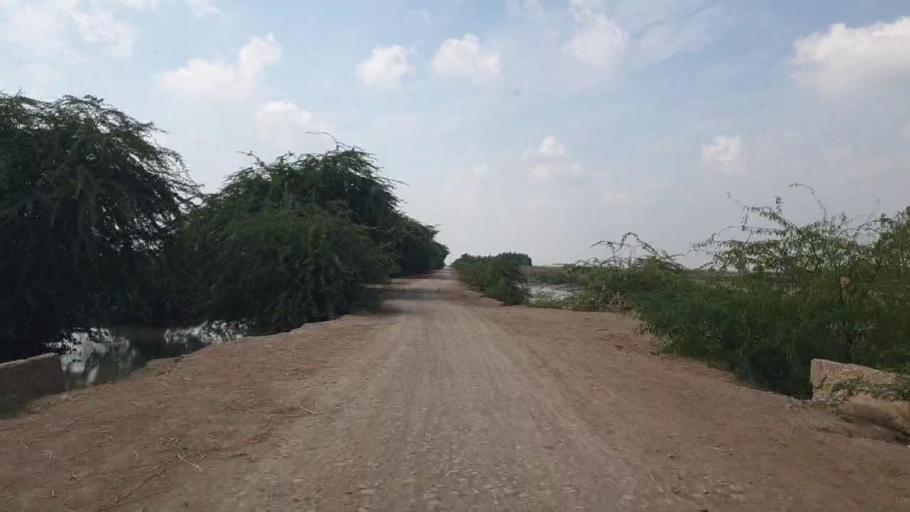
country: PK
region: Sindh
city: Badin
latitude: 24.5066
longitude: 68.6420
